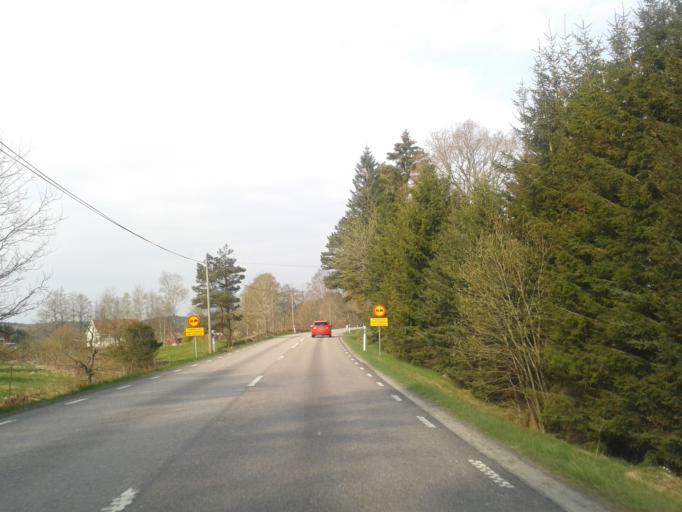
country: SE
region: Vaestra Goetaland
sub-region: Kungalvs Kommun
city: Kode
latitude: 57.8925
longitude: 11.8629
